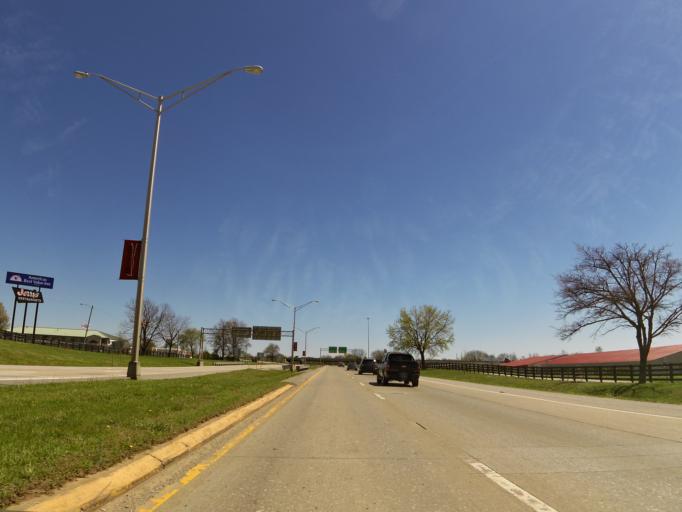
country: US
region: Kentucky
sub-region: Warren County
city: Bowling Green
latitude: 37.0076
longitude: -86.3736
